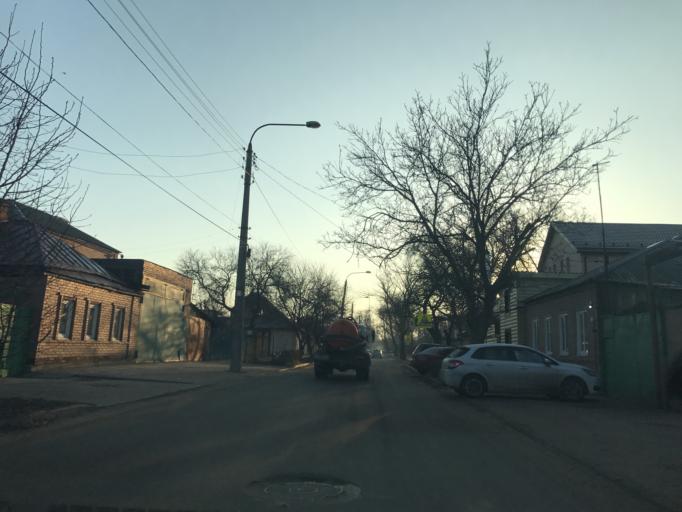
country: RU
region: Rostov
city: Rostov-na-Donu
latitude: 47.2141
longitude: 39.6540
